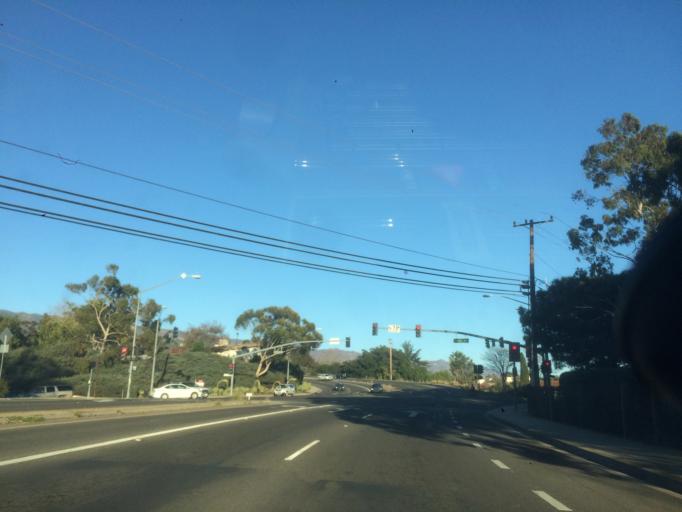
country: US
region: California
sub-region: Santa Barbara County
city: Mission Canyon
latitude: 34.4257
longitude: -119.7357
